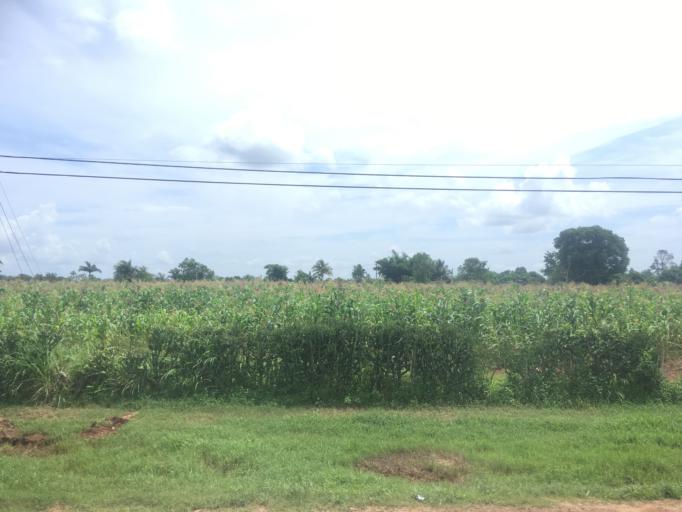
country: CU
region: Matanzas
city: Perico
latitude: 22.7779
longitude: -81.0354
